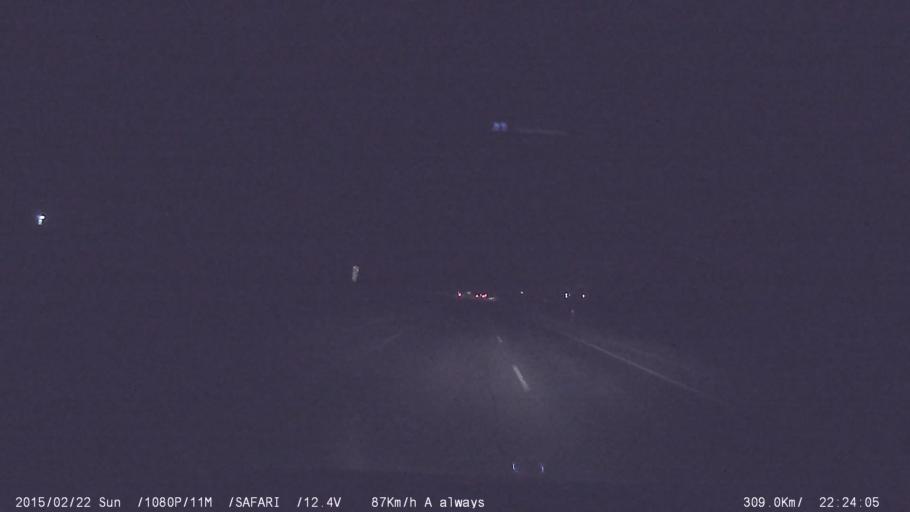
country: IN
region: Tamil Nadu
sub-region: Karur
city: Karur
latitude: 11.0332
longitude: 78.0632
